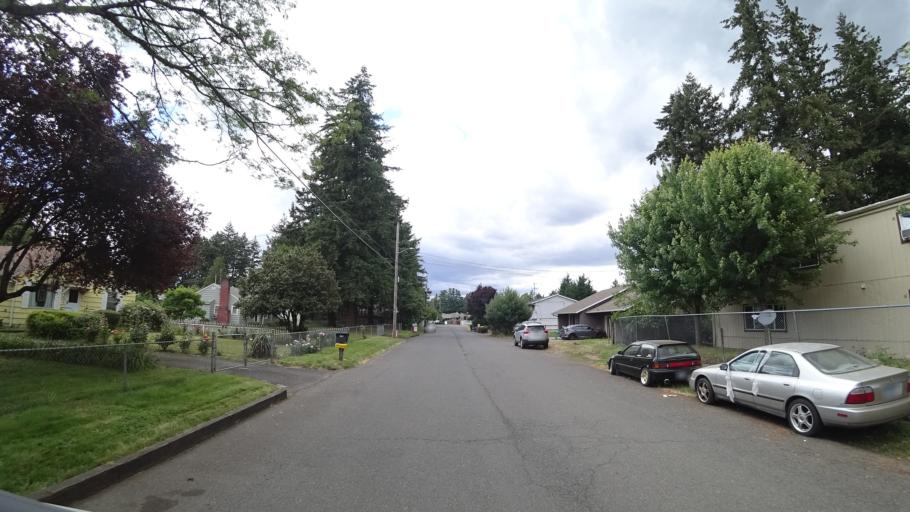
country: US
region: Oregon
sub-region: Multnomah County
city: Lents
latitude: 45.4974
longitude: -122.5216
